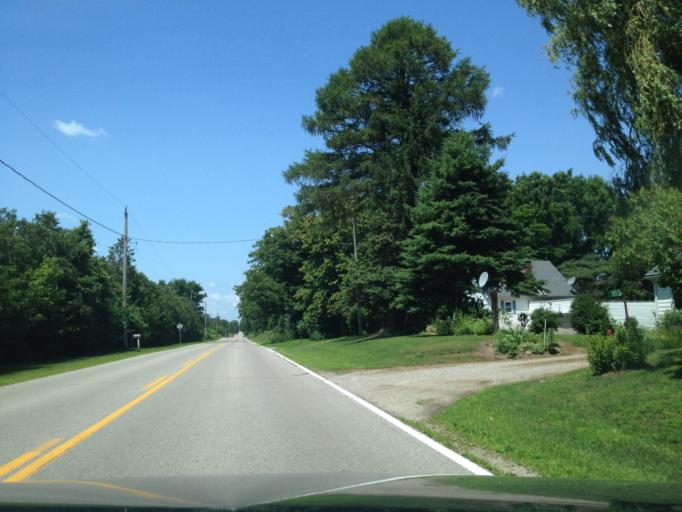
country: CA
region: Ontario
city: Aylmer
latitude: 42.6174
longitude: -80.7066
